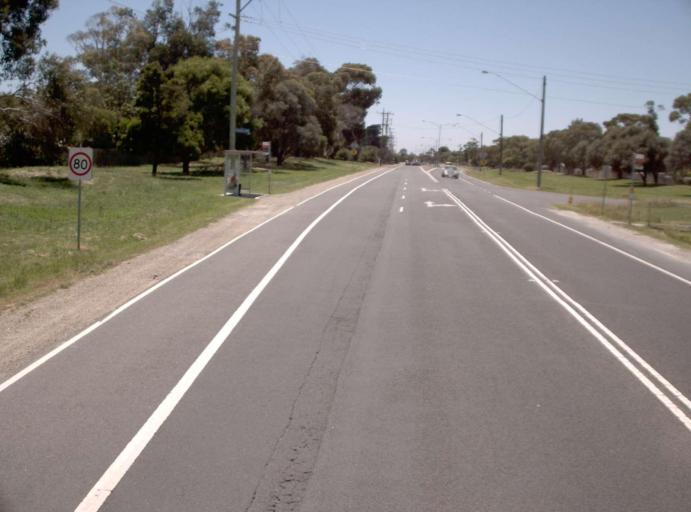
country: AU
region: Victoria
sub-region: Mornington Peninsula
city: Mount Martha
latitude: -38.2519
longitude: 145.0364
